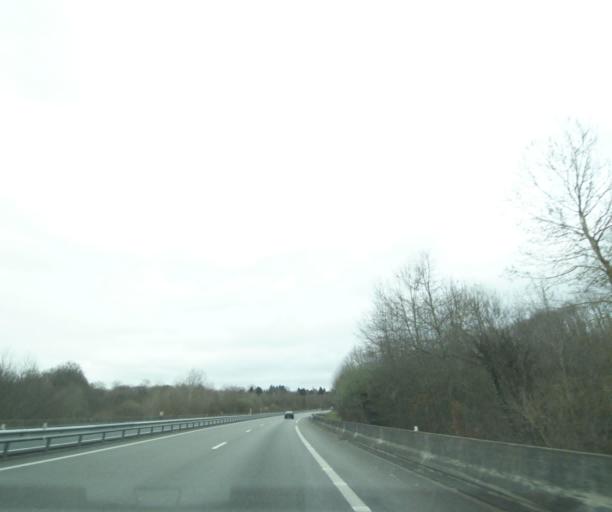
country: FR
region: Limousin
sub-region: Departement de la Correze
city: Uzerche
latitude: 45.4067
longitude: 1.5537
